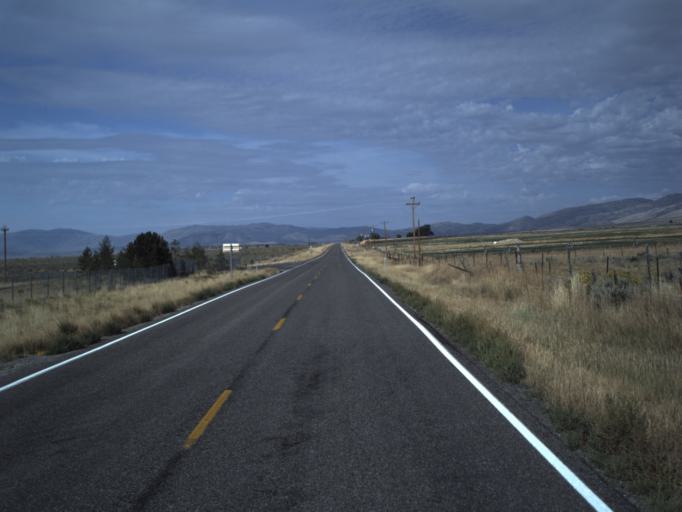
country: US
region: Idaho
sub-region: Cassia County
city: Burley
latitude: 41.8170
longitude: -113.3331
